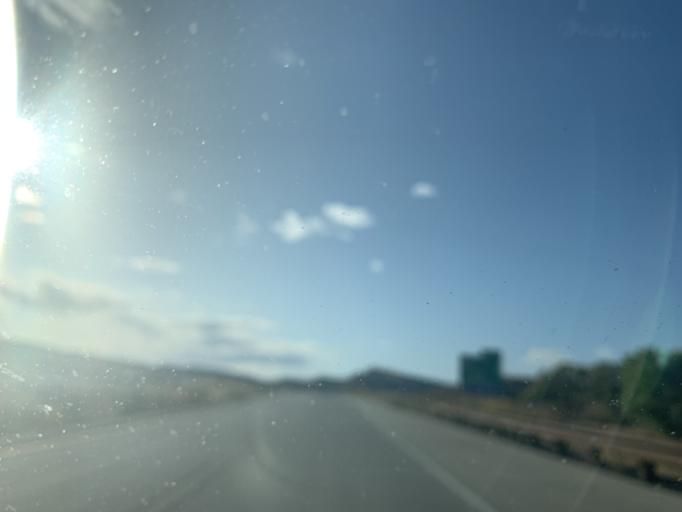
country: US
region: Colorado
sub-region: Mesa County
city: Loma
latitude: 39.1780
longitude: -108.8074
